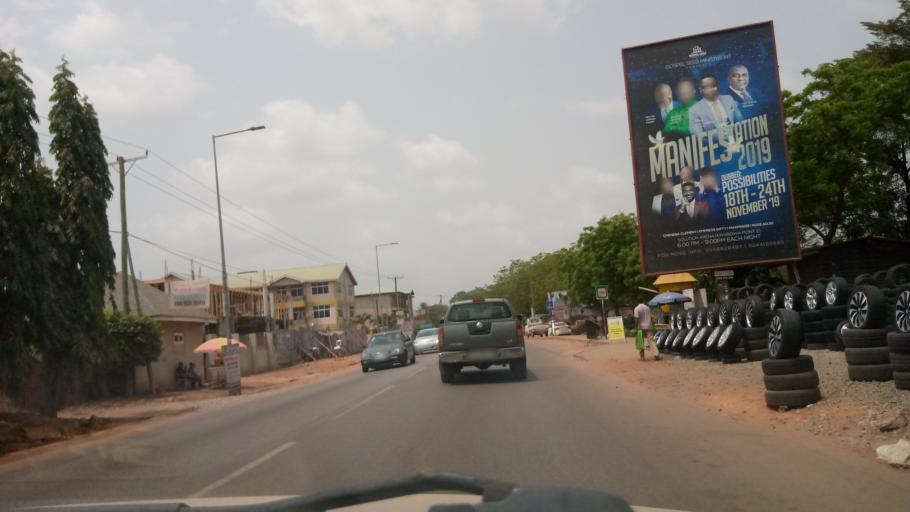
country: GH
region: Greater Accra
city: Dome
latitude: 5.6676
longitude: -0.2153
